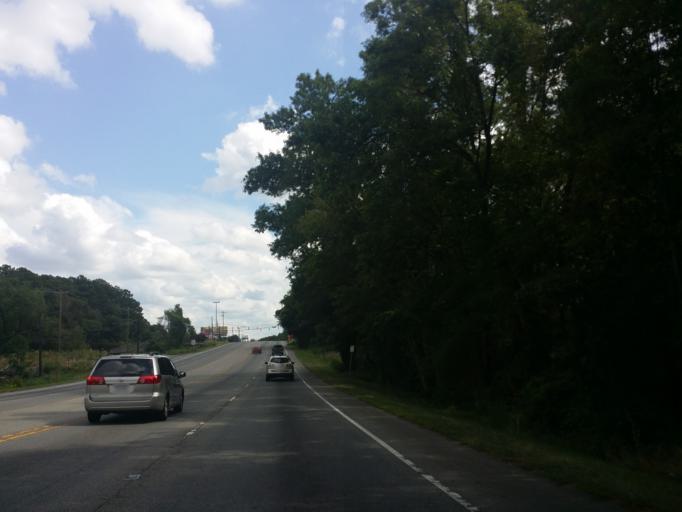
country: US
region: North Carolina
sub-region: Durham County
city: Durham
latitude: 35.9678
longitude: -78.8480
